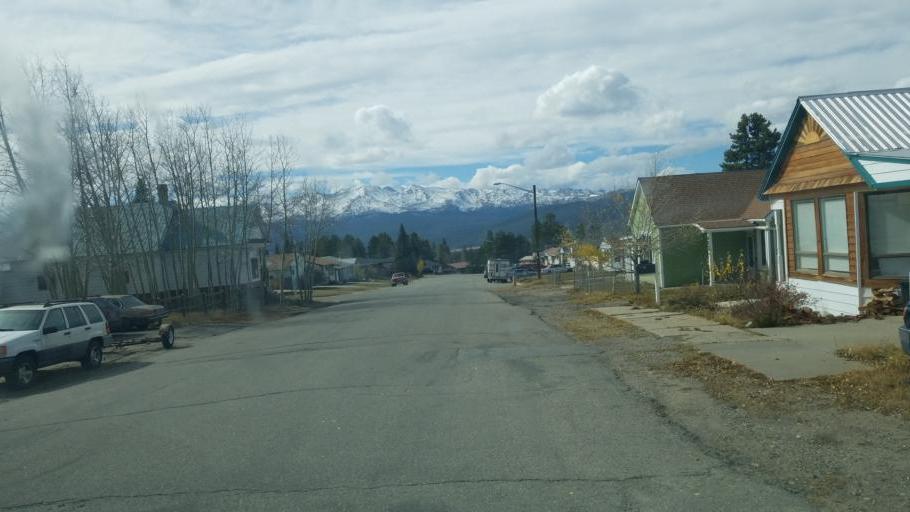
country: US
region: Colorado
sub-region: Lake County
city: Leadville
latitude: 39.2479
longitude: -106.2999
